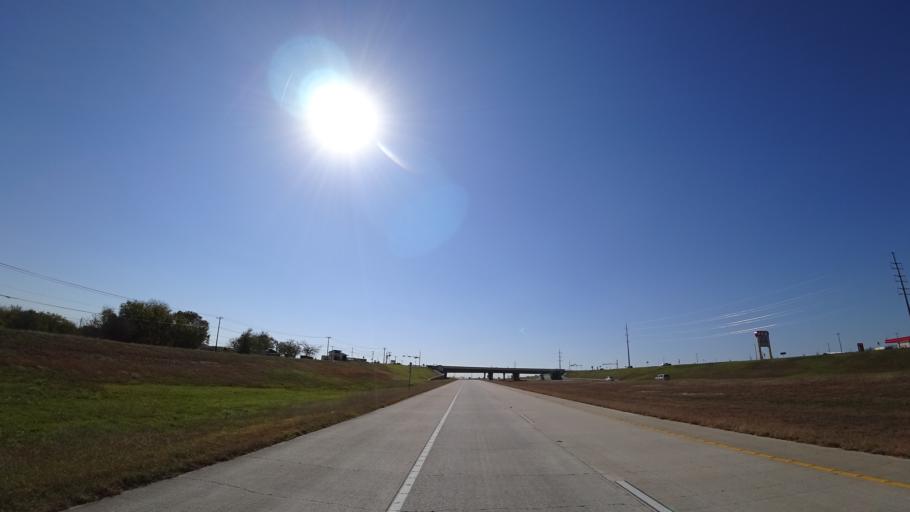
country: US
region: Texas
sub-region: Williamson County
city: Hutto
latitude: 30.5027
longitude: -97.5794
